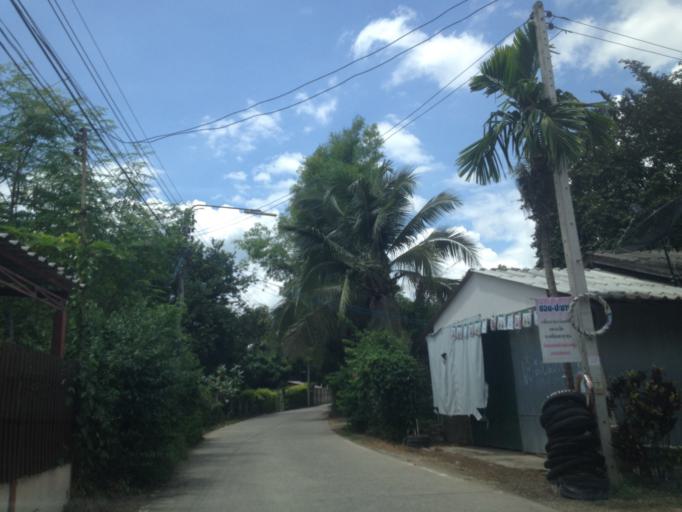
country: TH
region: Chiang Mai
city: Hang Dong
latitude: 18.6902
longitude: 98.8913
